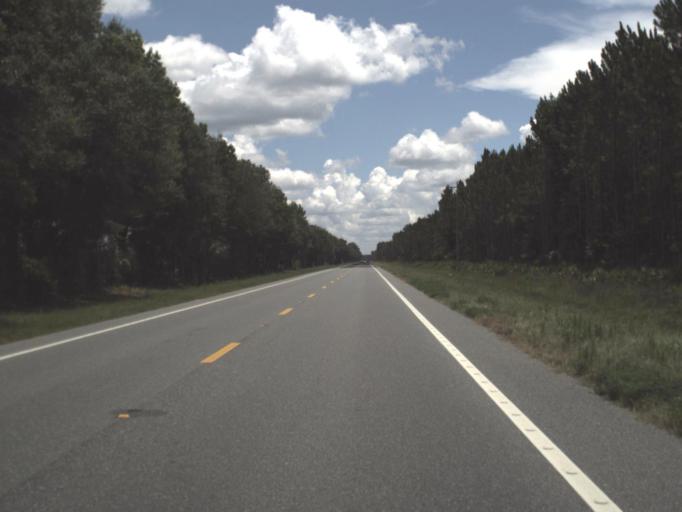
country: US
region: Florida
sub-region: Taylor County
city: Perry
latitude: 30.1411
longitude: -83.9127
